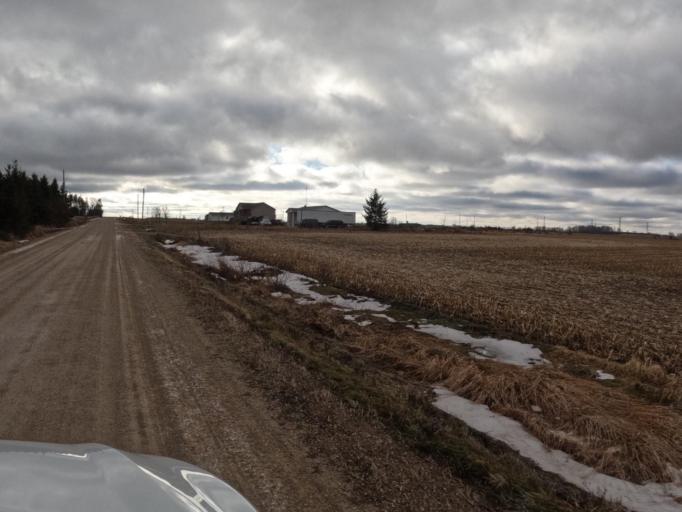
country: CA
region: Ontario
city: Shelburne
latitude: 44.0060
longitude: -80.3883
